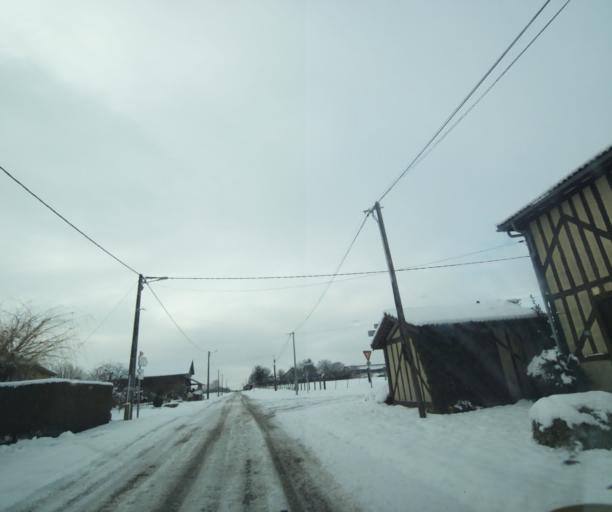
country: FR
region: Champagne-Ardenne
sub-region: Departement de la Haute-Marne
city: Montier-en-Der
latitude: 48.5217
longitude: 4.7035
